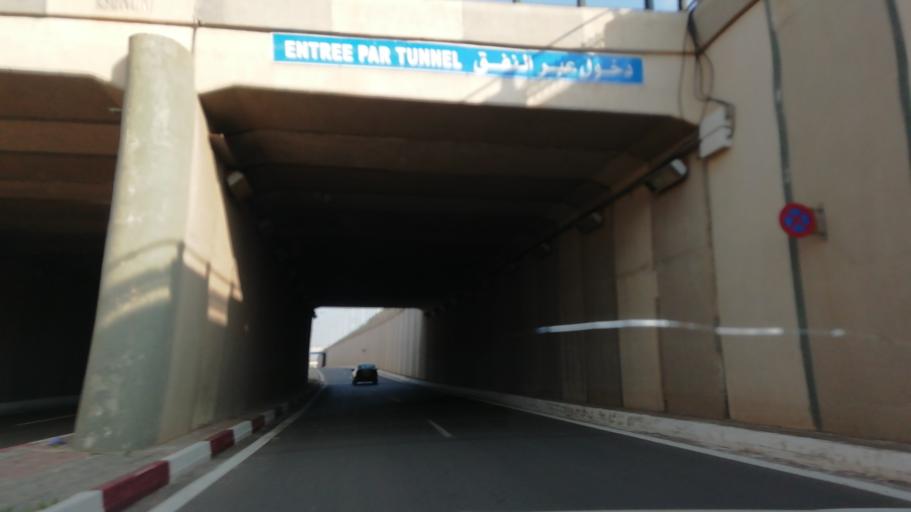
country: DZ
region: Ain Temouchent
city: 'Ain Temouchent
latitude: 35.2911
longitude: -1.1252
